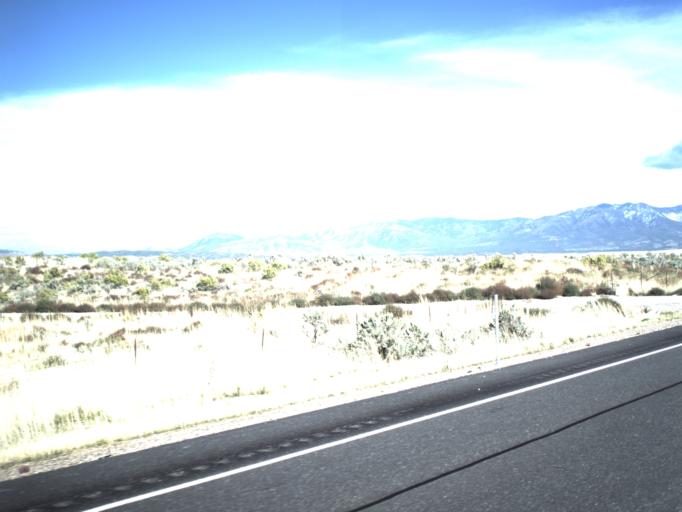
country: US
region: Utah
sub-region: Millard County
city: Fillmore
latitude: 39.1385
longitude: -112.3702
